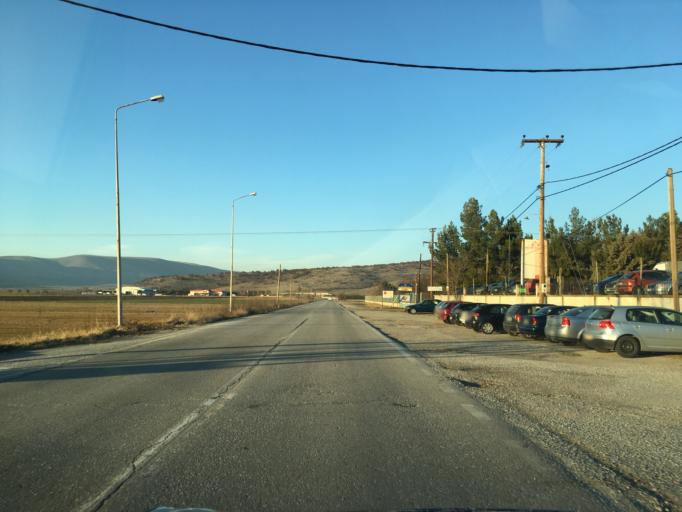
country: GR
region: West Macedonia
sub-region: Nomos Kozanis
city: Kozani
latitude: 40.2970
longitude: 21.7346
